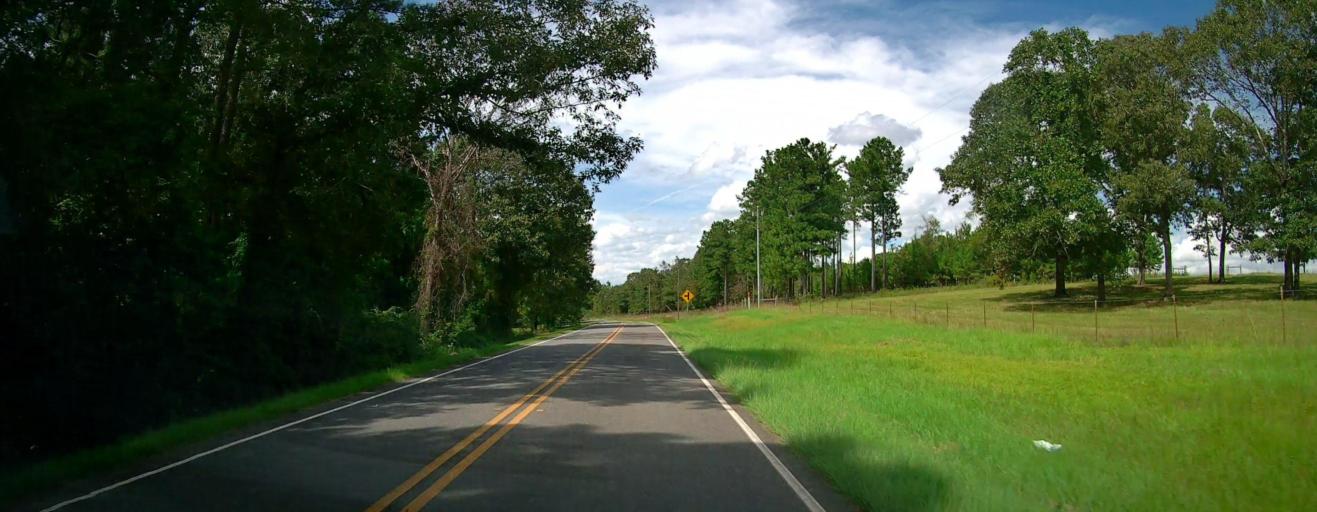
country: US
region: Georgia
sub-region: Taylor County
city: Butler
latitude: 32.5223
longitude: -84.2058
